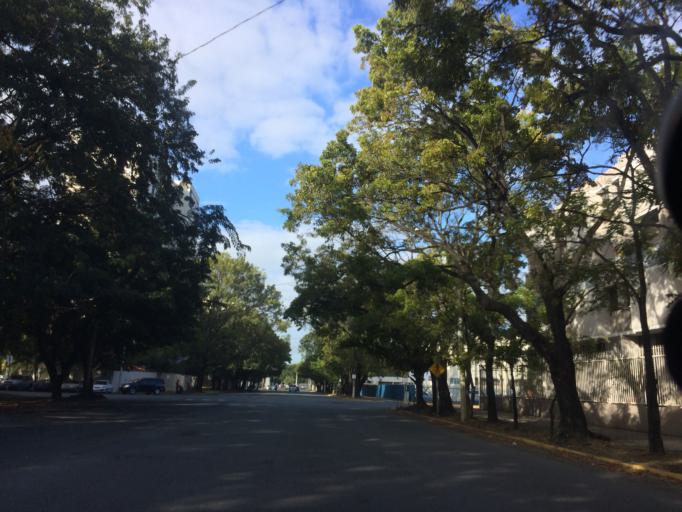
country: PR
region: Catano
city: Catano
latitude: 18.4283
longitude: -66.0654
